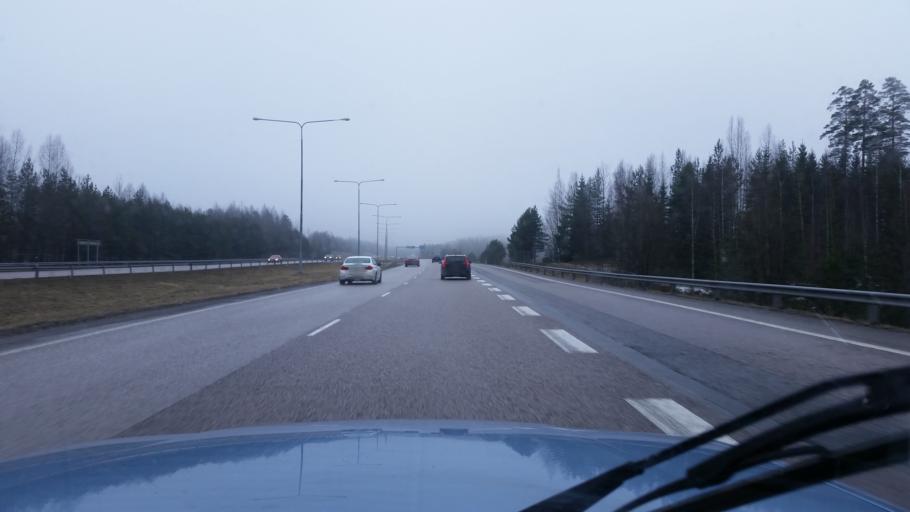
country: FI
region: Uusimaa
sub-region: Helsinki
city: Hyvinge
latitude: 60.5621
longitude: 24.8225
